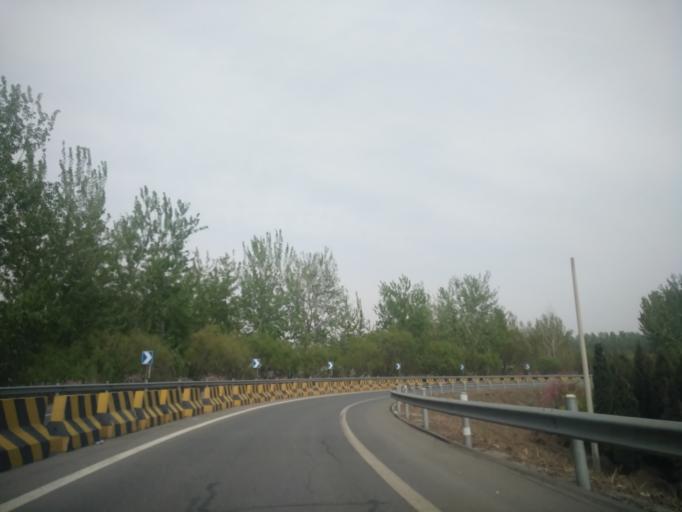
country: CN
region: Beijing
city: Xiji
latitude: 39.7974
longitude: 116.9958
